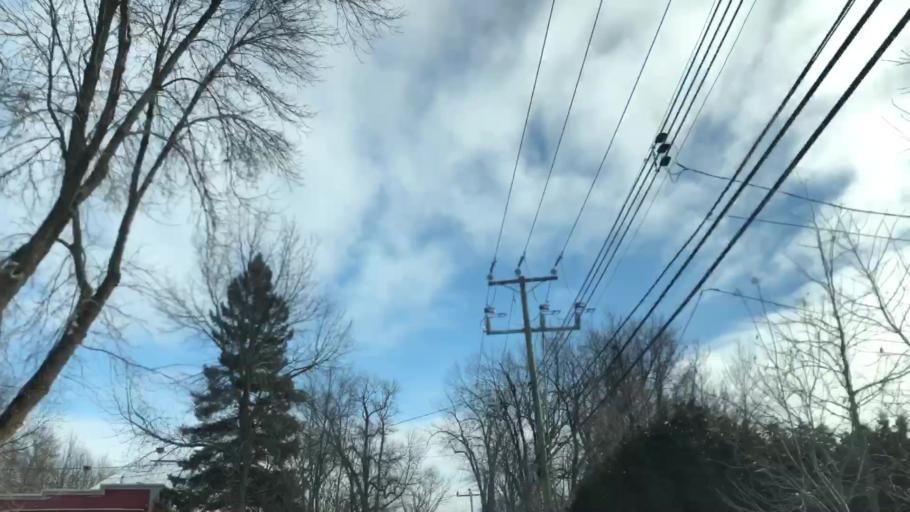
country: CA
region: Quebec
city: Sainte-Anne-de-Bellevue
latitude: 45.4188
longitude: -73.9657
